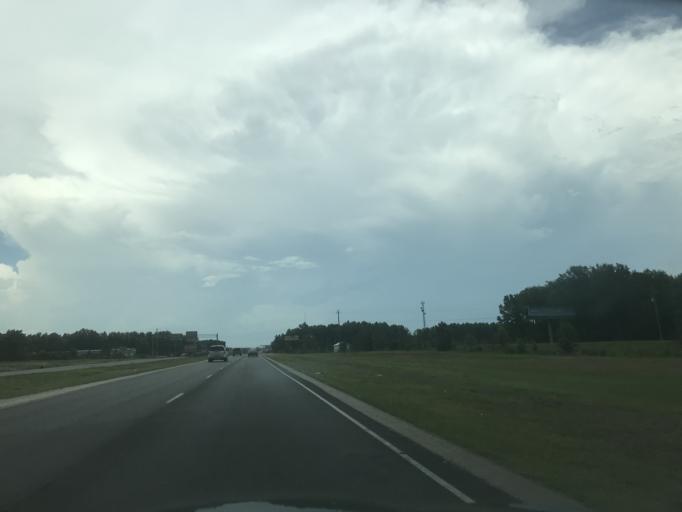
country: US
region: North Carolina
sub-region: Johnston County
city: Clayton
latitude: 35.6037
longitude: -78.4154
